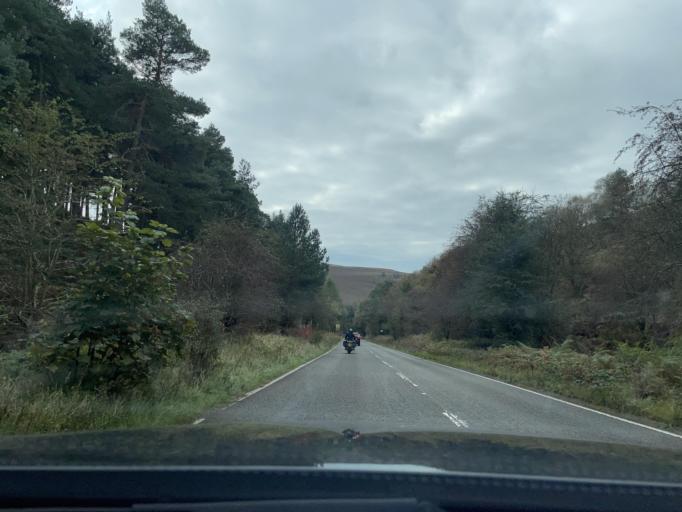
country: GB
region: England
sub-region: Derbyshire
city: Hathersage
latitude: 53.3810
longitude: -1.6824
